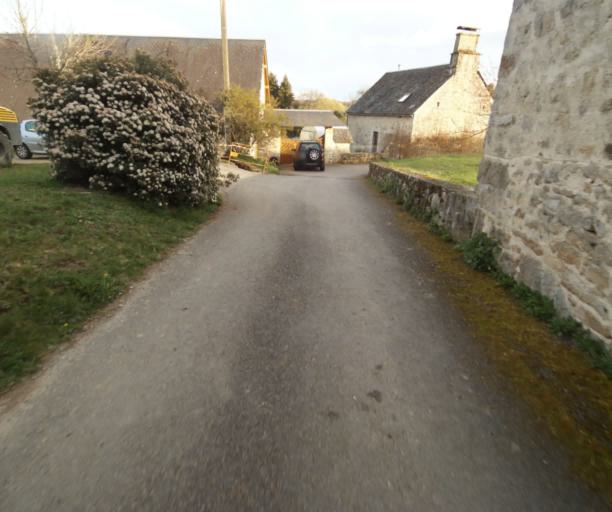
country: FR
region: Limousin
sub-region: Departement de la Correze
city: Argentat
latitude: 45.2211
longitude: 1.9800
